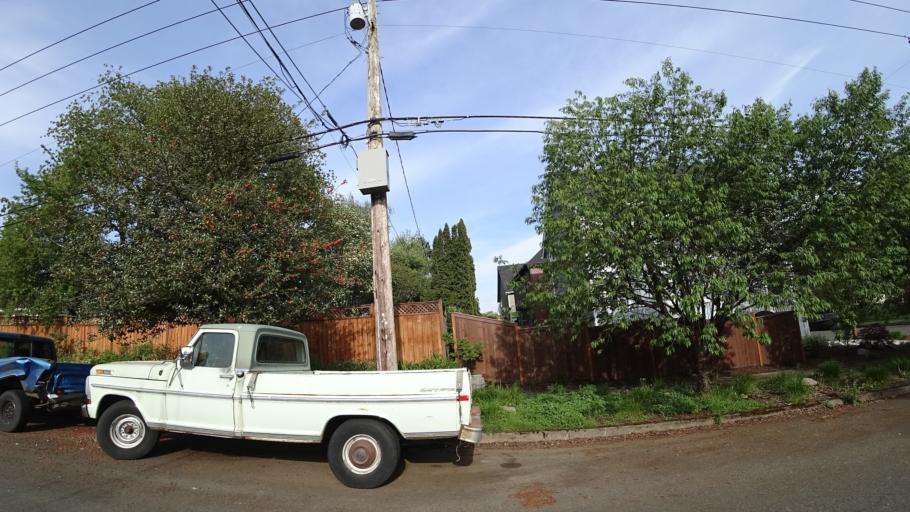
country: US
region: Oregon
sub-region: Clackamas County
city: Milwaukie
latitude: 45.4666
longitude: -122.6194
